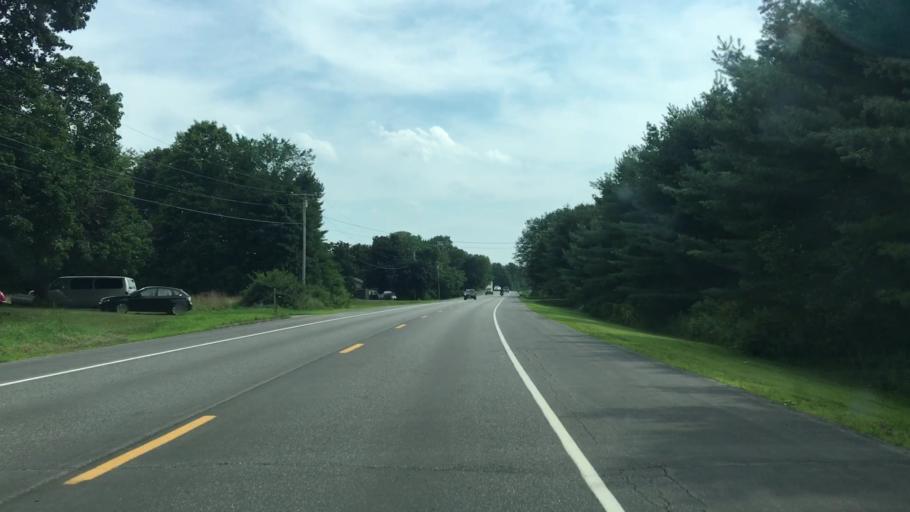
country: US
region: Maine
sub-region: Kennebec County
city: Windsor
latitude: 44.3880
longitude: -69.5705
